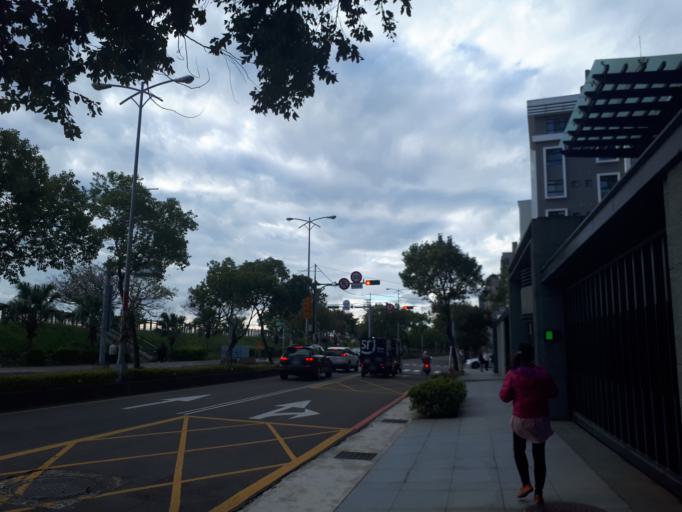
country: TW
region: Taiwan
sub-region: Hsinchu
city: Zhubei
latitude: 24.8010
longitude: 121.0354
